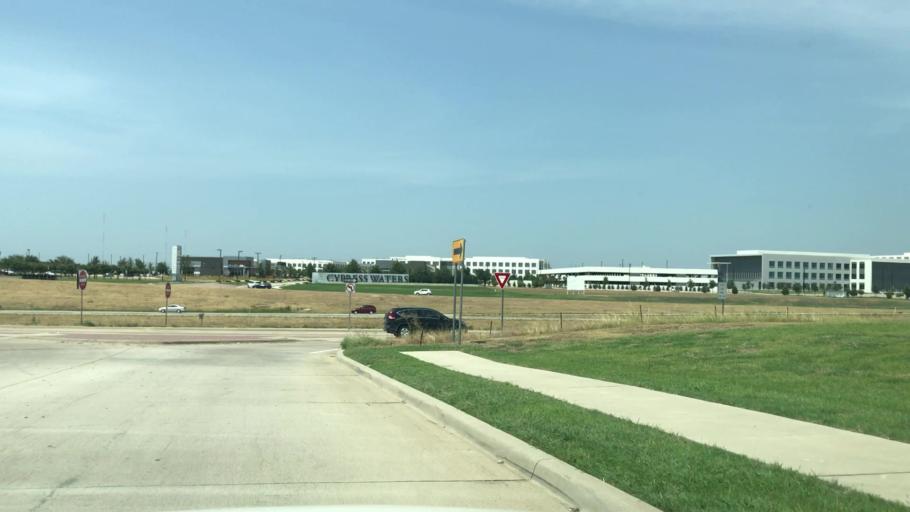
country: US
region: Texas
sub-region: Dallas County
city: Coppell
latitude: 32.9218
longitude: -96.9915
